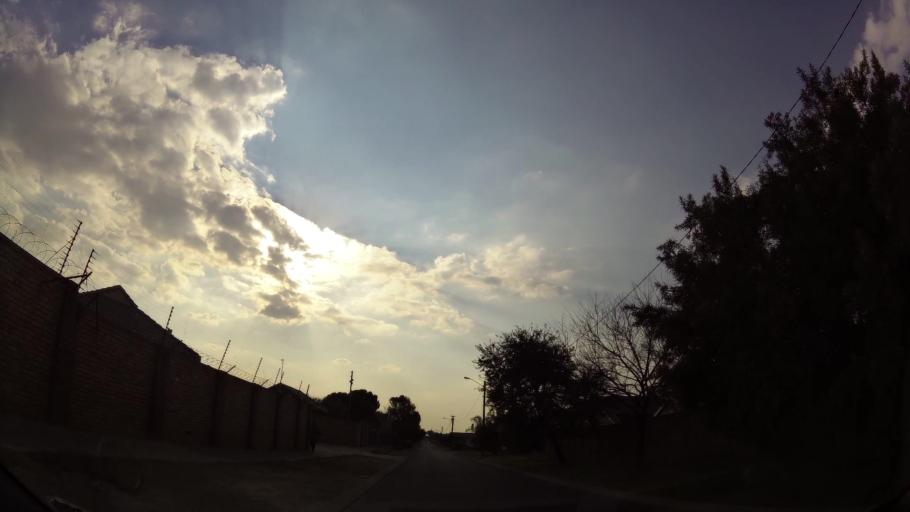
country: ZA
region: Gauteng
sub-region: Ekurhuleni Metropolitan Municipality
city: Benoni
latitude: -26.1135
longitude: 28.2885
